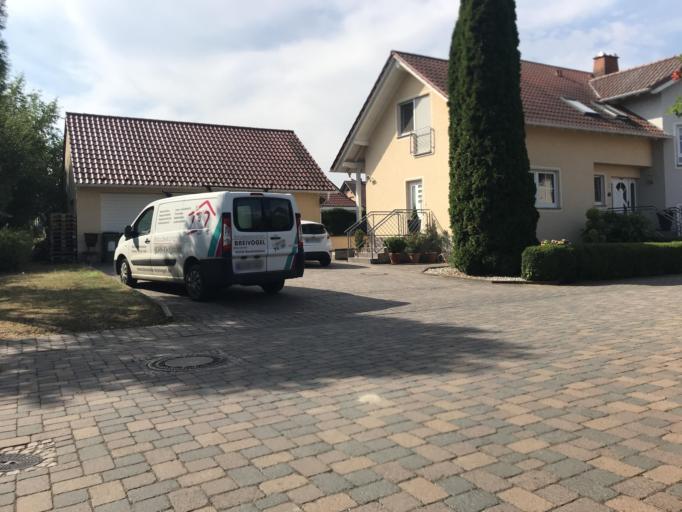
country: DE
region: Rheinland-Pfalz
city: Bechtolsheim
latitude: 49.8050
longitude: 8.1994
